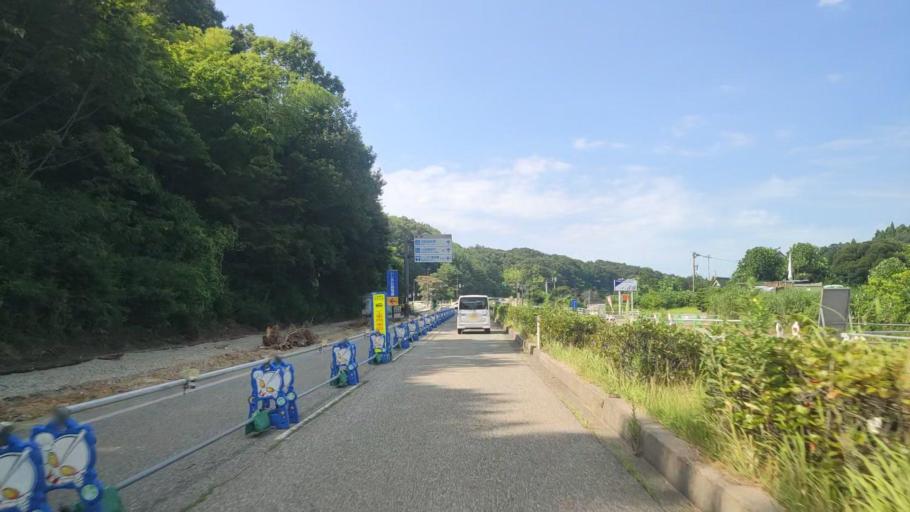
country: JP
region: Ishikawa
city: Matsuto
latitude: 36.4373
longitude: 136.5430
